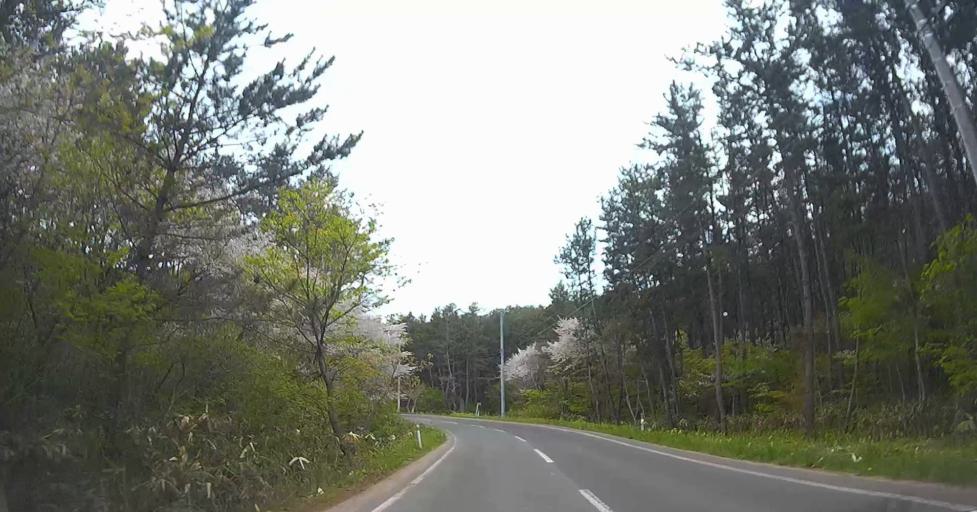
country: JP
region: Aomori
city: Shimokizukuri
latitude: 40.9374
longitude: 140.3345
